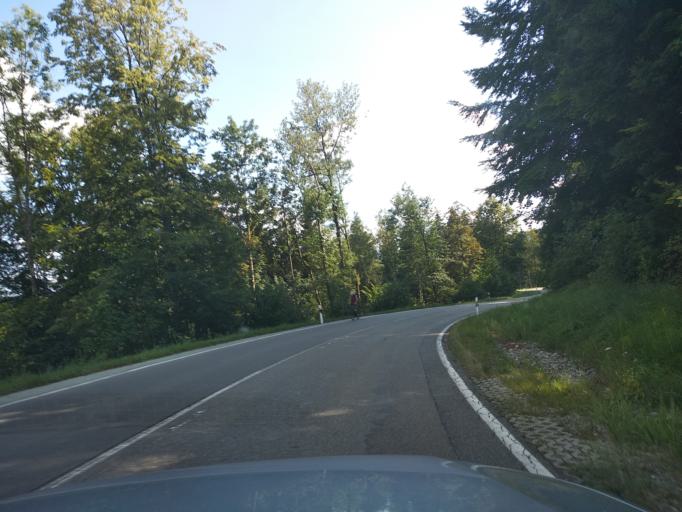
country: DE
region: Baden-Wuerttemberg
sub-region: Tuebingen Region
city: Leutkirch im Allgau
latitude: 47.8693
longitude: 10.0068
